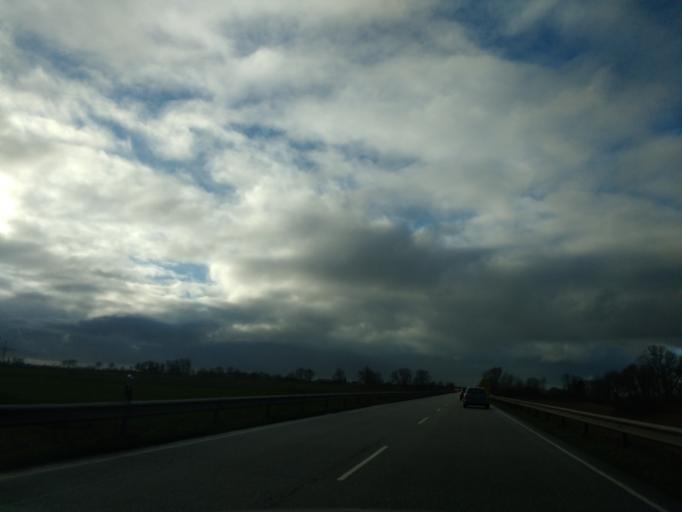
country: DE
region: Schleswig-Holstein
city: Bekmunde
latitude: 53.9372
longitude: 9.4396
